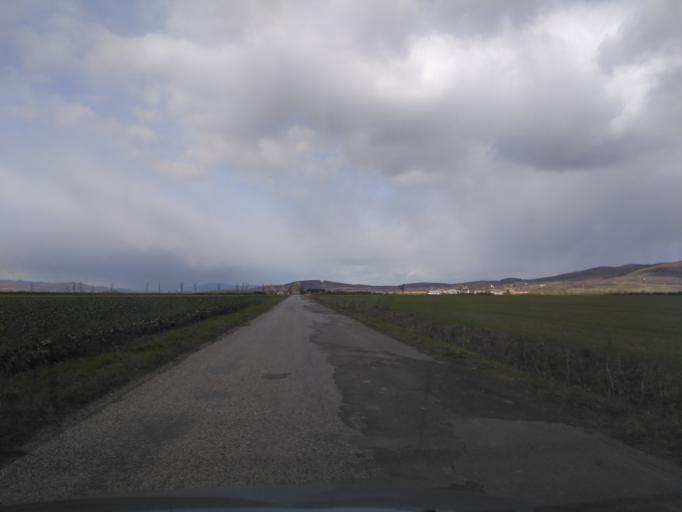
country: HU
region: Borsod-Abauj-Zemplen
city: Satoraljaujhely
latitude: 48.4150
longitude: 21.6792
